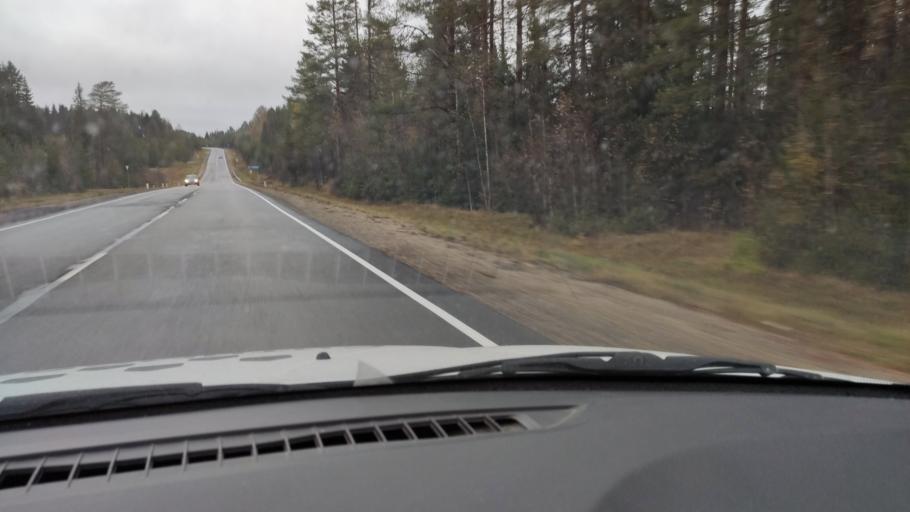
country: RU
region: Kirov
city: Chernaya Kholunitsa
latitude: 58.8458
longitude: 51.7458
